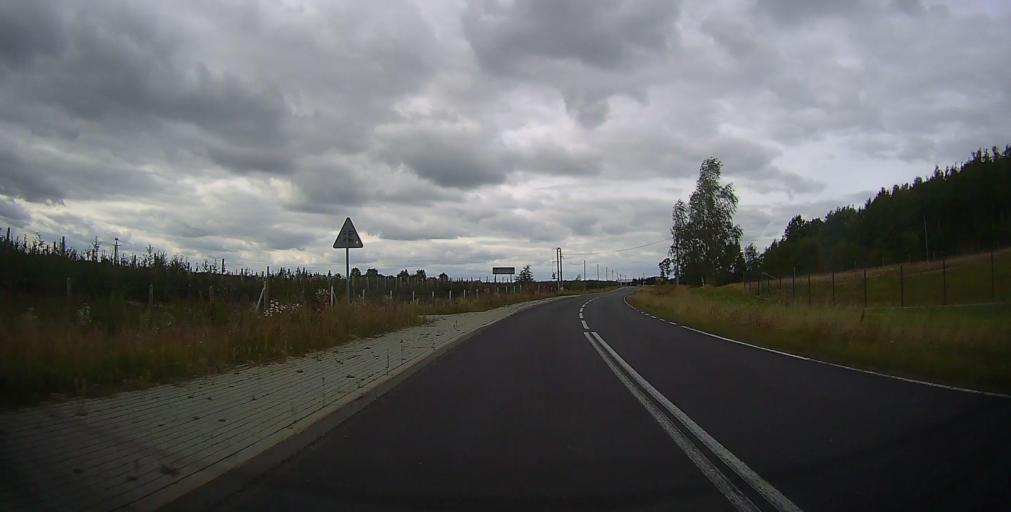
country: PL
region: Masovian Voivodeship
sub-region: Powiat grojecki
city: Goszczyn
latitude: 51.7608
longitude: 20.9008
